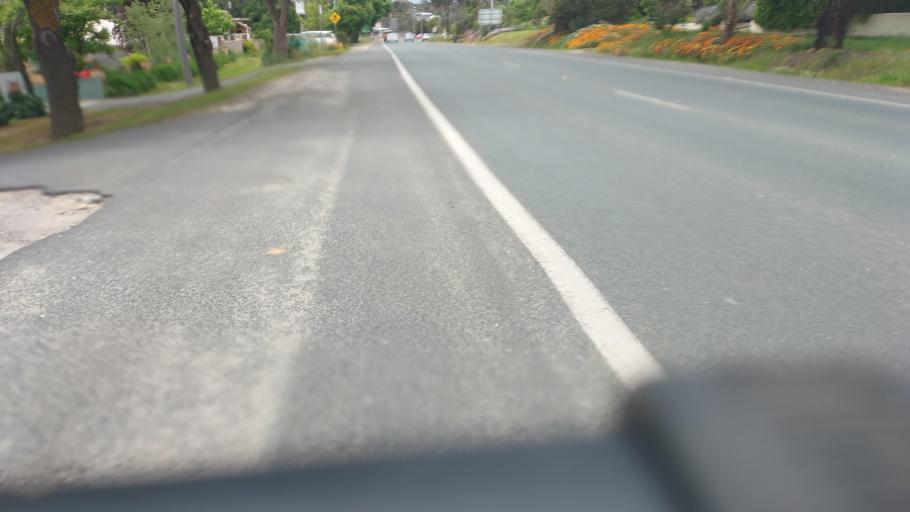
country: AU
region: Victoria
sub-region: Mount Alexander
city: Castlemaine
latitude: -37.0749
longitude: 144.2045
